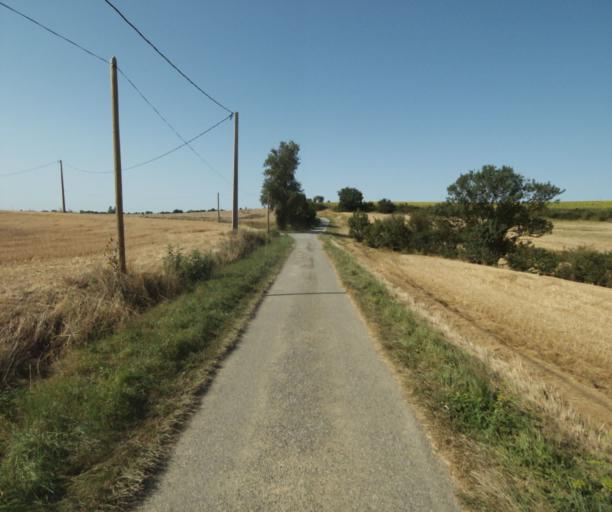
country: FR
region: Midi-Pyrenees
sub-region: Departement de la Haute-Garonne
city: Avignonet-Lauragais
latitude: 43.4186
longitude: 1.8165
